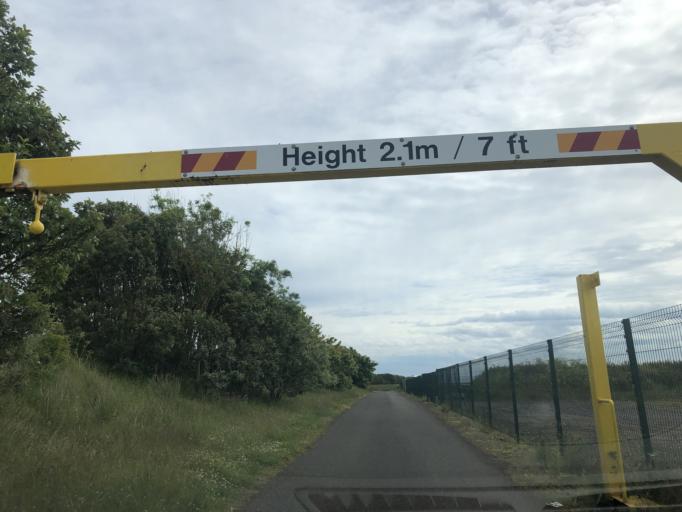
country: GB
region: Scotland
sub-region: Fife
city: Anstruther
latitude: 56.2748
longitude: -2.6038
